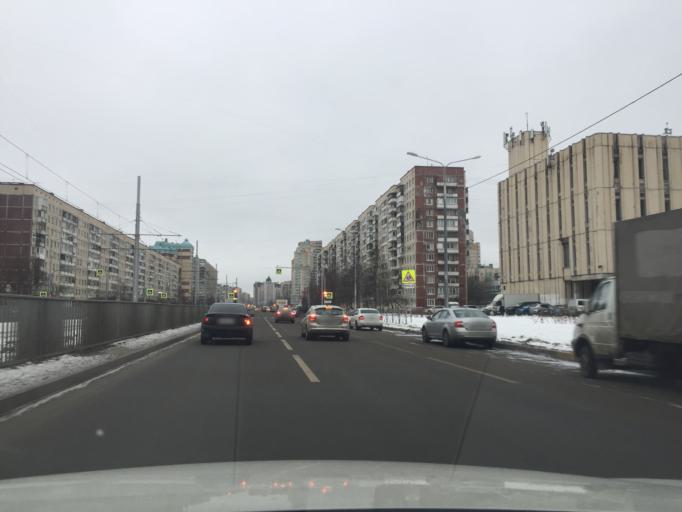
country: RU
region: St.-Petersburg
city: Krasnogvargeisky
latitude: 59.9575
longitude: 30.4791
